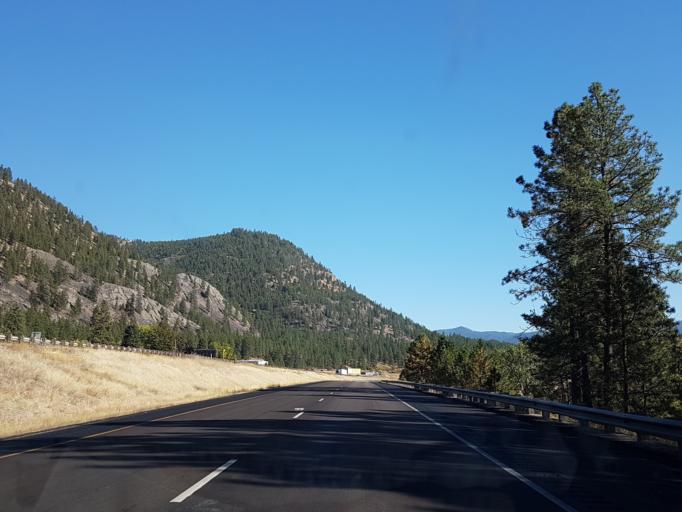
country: US
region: Montana
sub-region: Missoula County
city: Frenchtown
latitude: 47.0190
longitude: -114.5161
